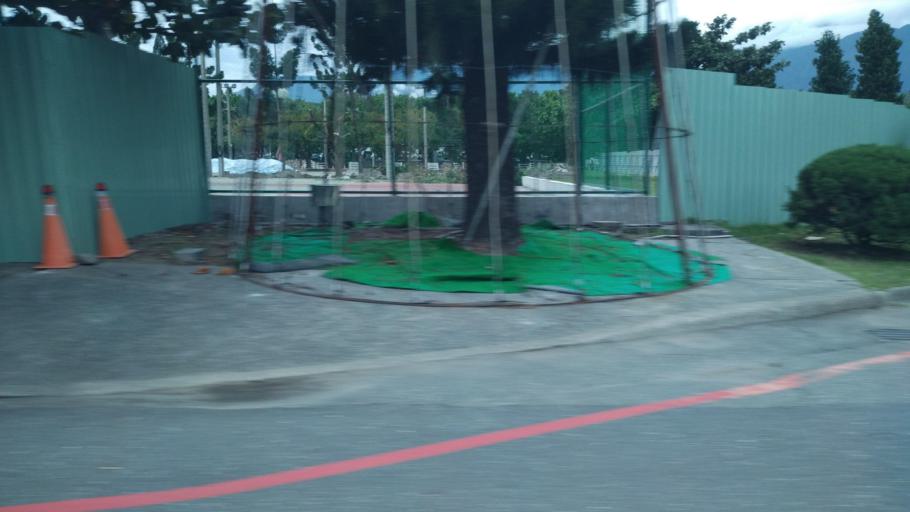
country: TW
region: Taiwan
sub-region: Hualien
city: Hualian
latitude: 23.9910
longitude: 121.6217
